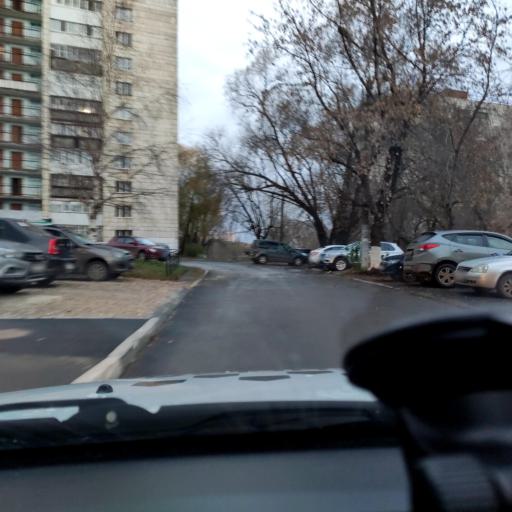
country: RU
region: Perm
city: Perm
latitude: 57.9795
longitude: 56.2332
